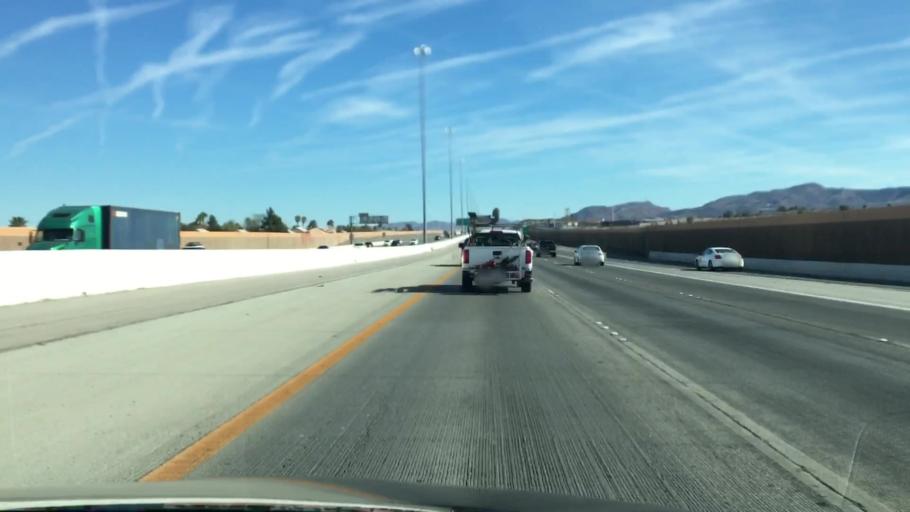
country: US
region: Nevada
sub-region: Clark County
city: Whitney
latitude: 36.0234
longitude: -115.1150
